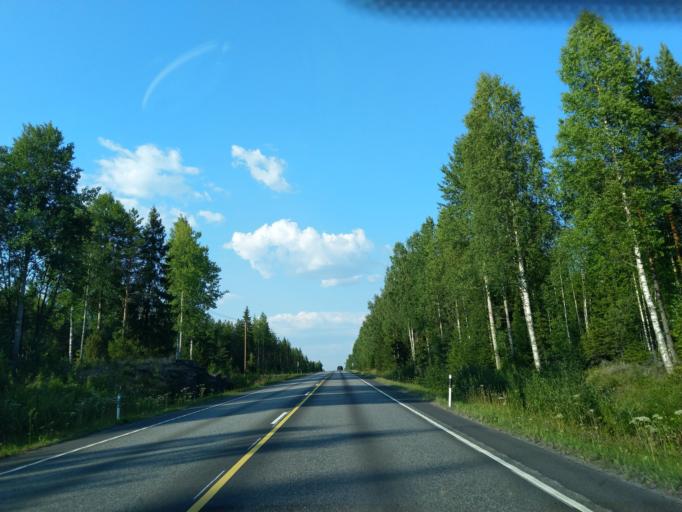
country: FI
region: Satakunta
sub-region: Pori
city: Pomarkku
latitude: 61.7194
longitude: 22.0513
